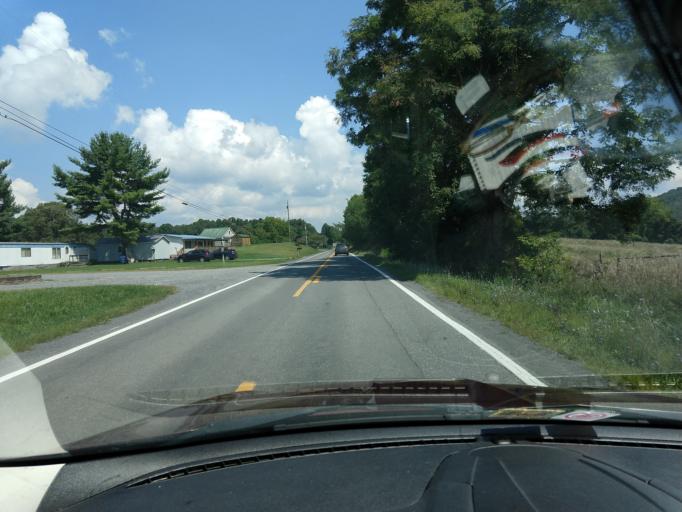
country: US
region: West Virginia
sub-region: Greenbrier County
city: Lewisburg
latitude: 37.8500
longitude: -80.5502
